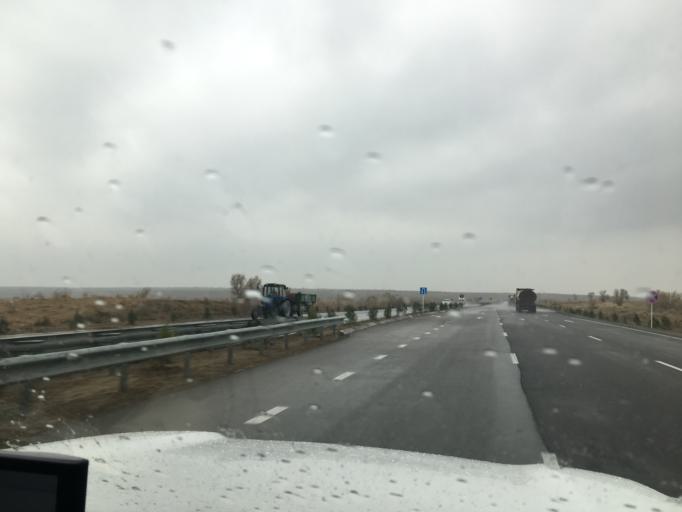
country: TM
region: Ahal
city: Annau
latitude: 37.8729
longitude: 58.6511
